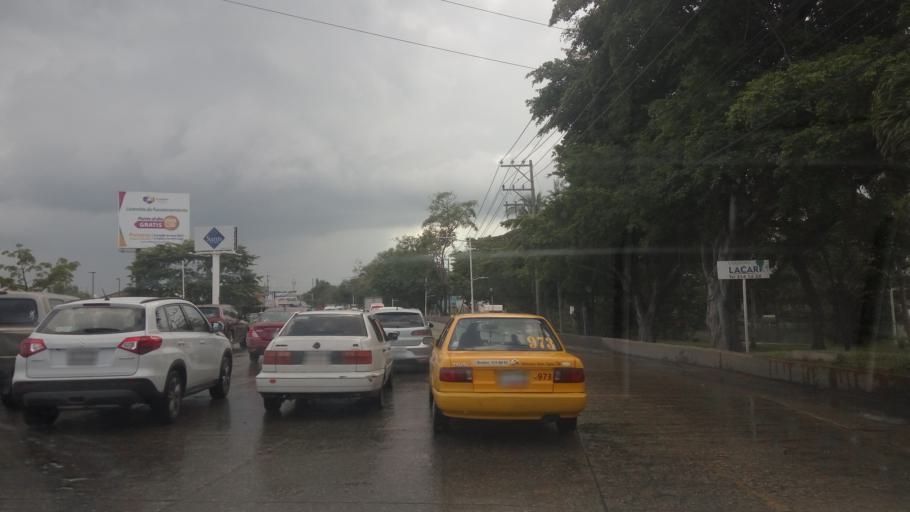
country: MX
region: Tabasco
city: Villahermosa
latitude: 18.0054
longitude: -92.9251
